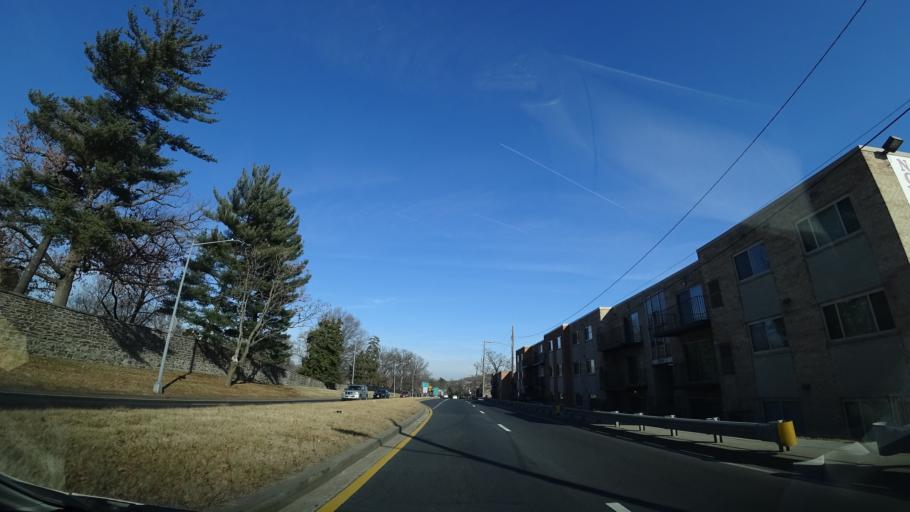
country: US
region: Maryland
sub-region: Prince George's County
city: Chillum
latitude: 38.9440
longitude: -77.0075
